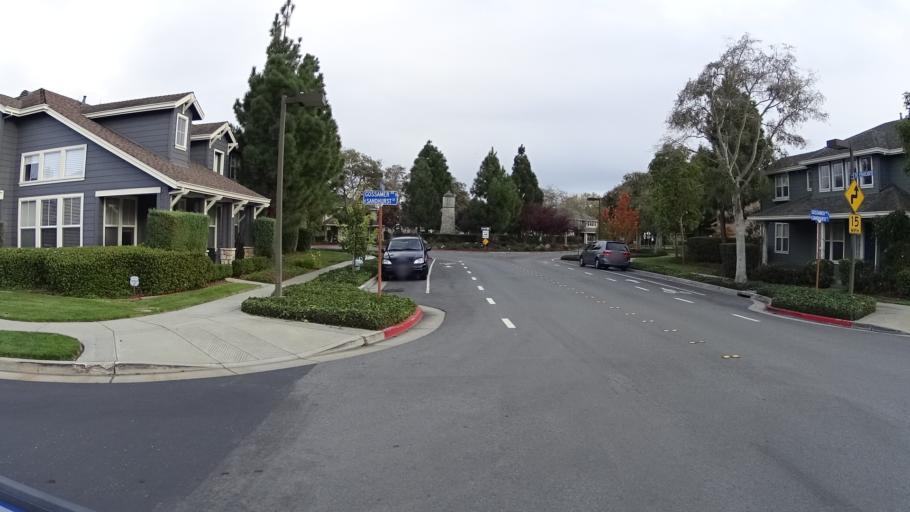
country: US
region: California
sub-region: San Mateo County
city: Redwood Shores
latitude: 37.5449
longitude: -122.2363
